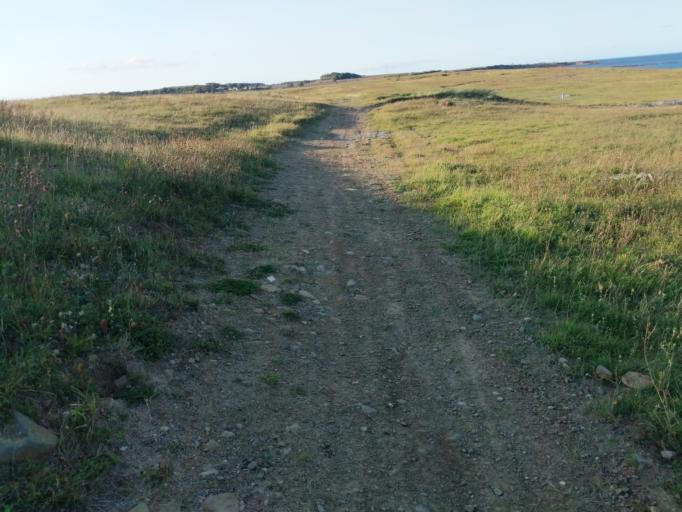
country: GB
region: England
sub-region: Northumberland
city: Lynemouth
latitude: 55.2115
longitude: -1.5262
